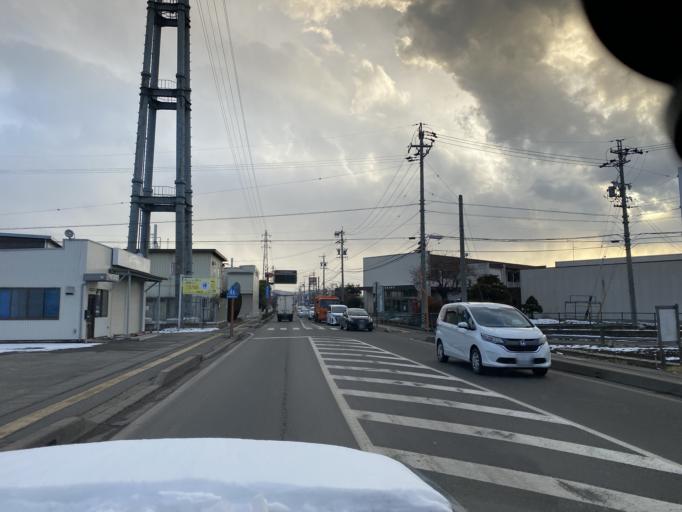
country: JP
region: Nagano
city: Nagano-shi
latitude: 36.6332
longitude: 138.2396
